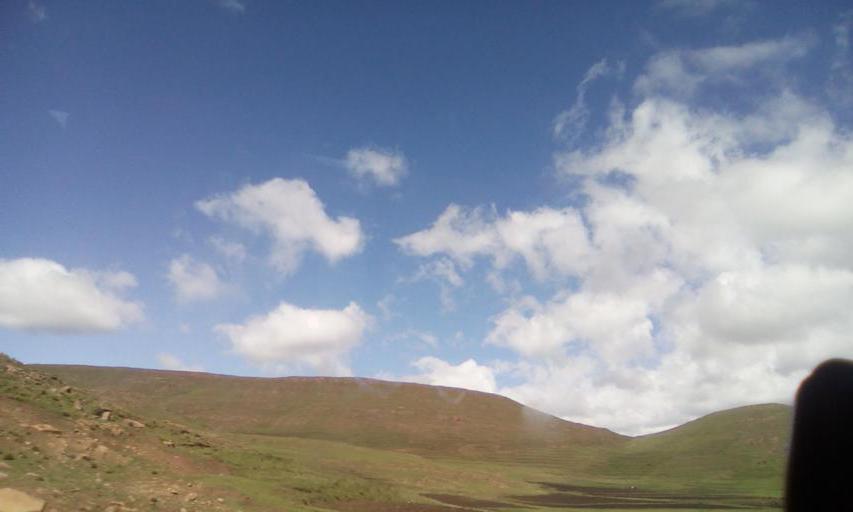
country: LS
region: Maseru
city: Nako
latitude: -29.8141
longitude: 28.0327
